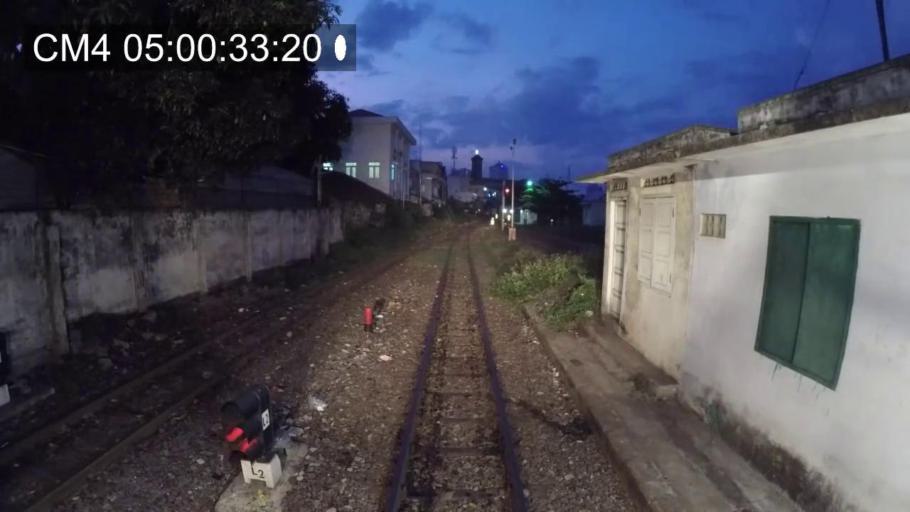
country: VN
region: Khanh Hoa
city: Nha Trang
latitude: 12.2451
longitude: 109.1877
